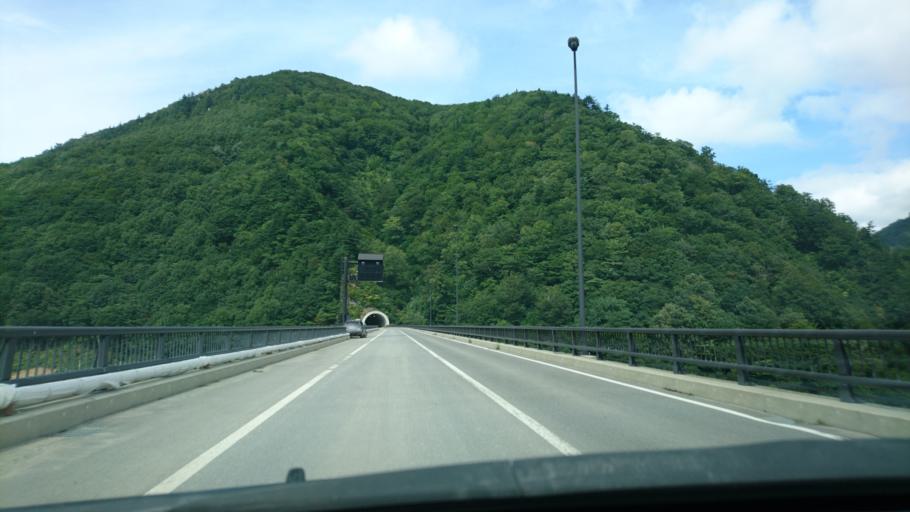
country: JP
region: Akita
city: Yuzawa
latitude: 39.0372
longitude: 140.7350
